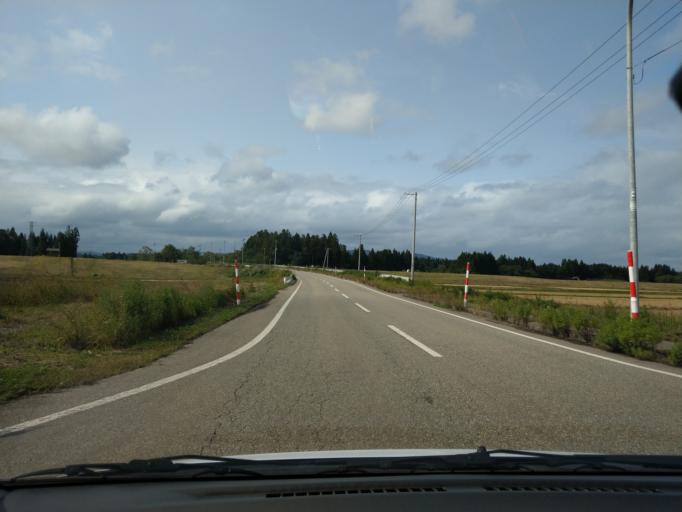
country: JP
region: Akita
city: Omagari
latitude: 39.5246
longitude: 140.2831
